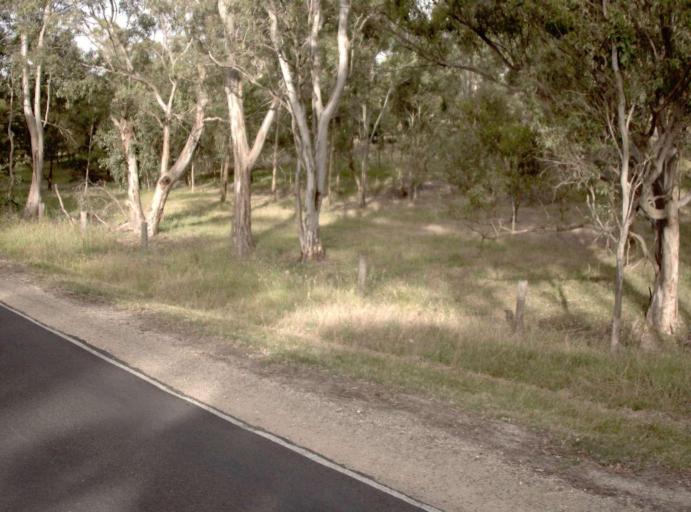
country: AU
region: Victoria
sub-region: Wellington
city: Sale
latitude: -37.9224
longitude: 146.9976
